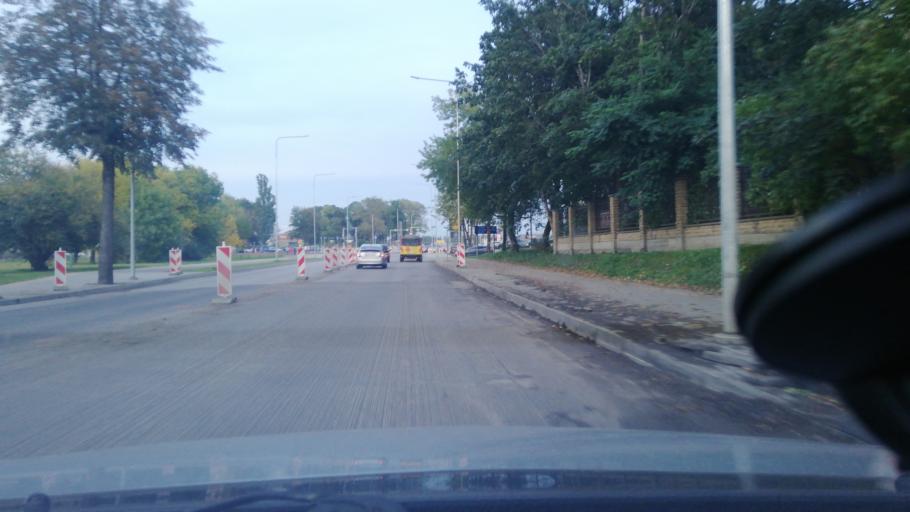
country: LT
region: Klaipedos apskritis
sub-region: Klaipeda
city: Klaipeda
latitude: 55.7045
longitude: 21.1573
